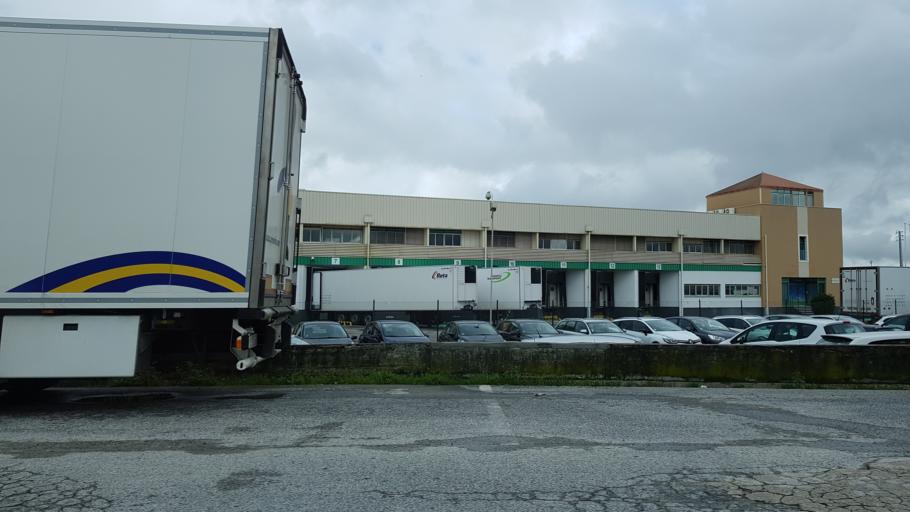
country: PT
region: Lisbon
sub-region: Alenquer
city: Carregado
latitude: 39.0303
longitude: -8.9665
